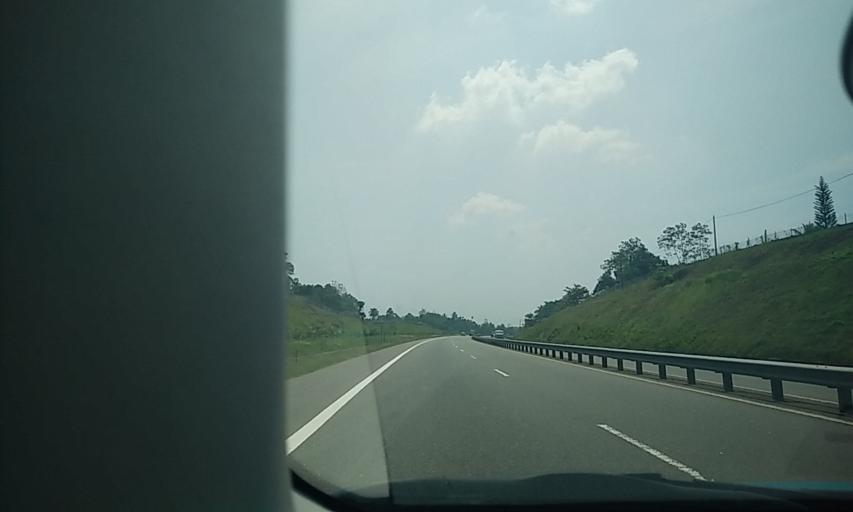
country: LK
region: Western
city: Horana South
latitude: 6.7489
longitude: 79.9968
